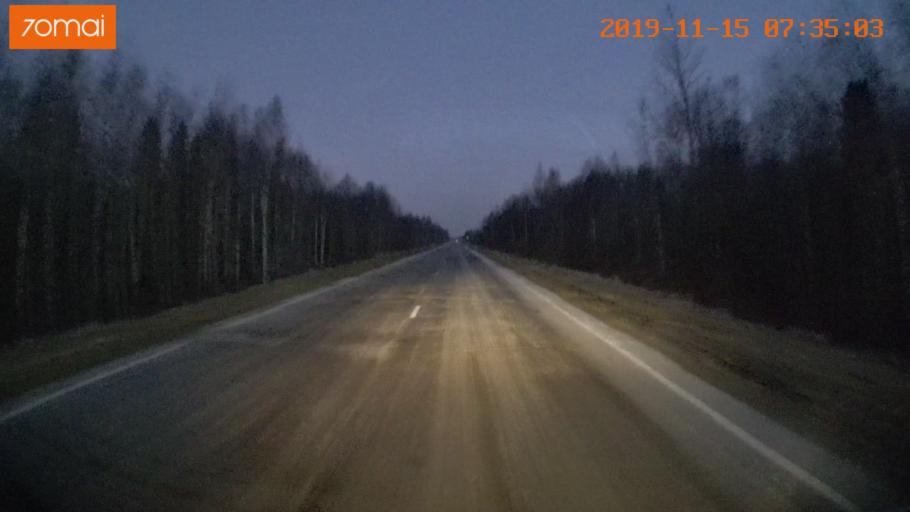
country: RU
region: Vologda
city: Sheksna
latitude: 58.7267
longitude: 38.4573
